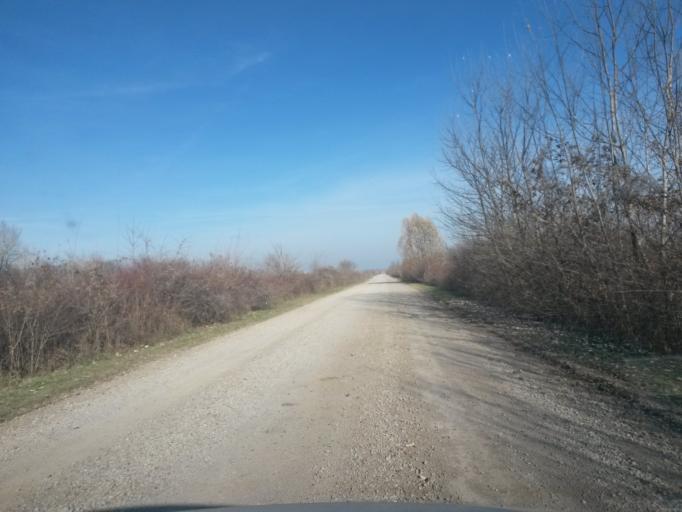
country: HR
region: Vukovarsko-Srijemska
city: Mirkovci
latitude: 45.2283
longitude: 18.8813
